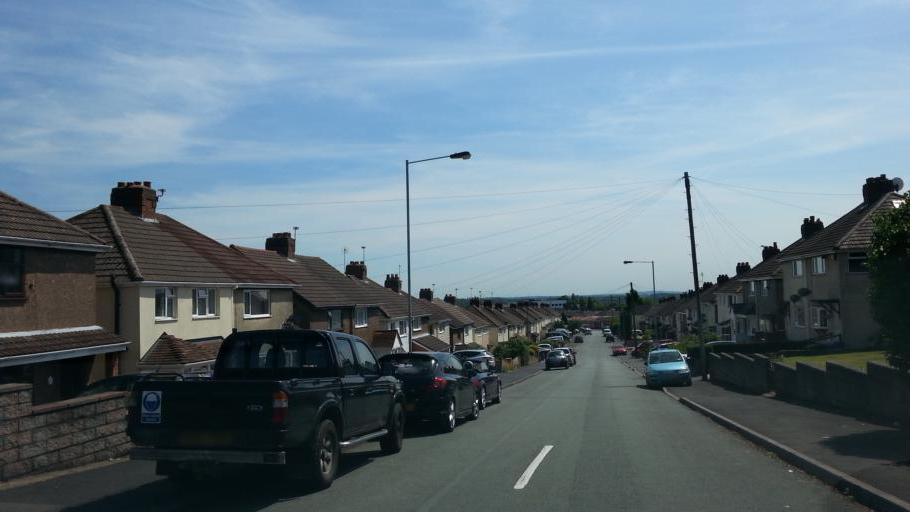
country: GB
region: England
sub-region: Staffordshire
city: Cannock
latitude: 52.7165
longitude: -2.0220
